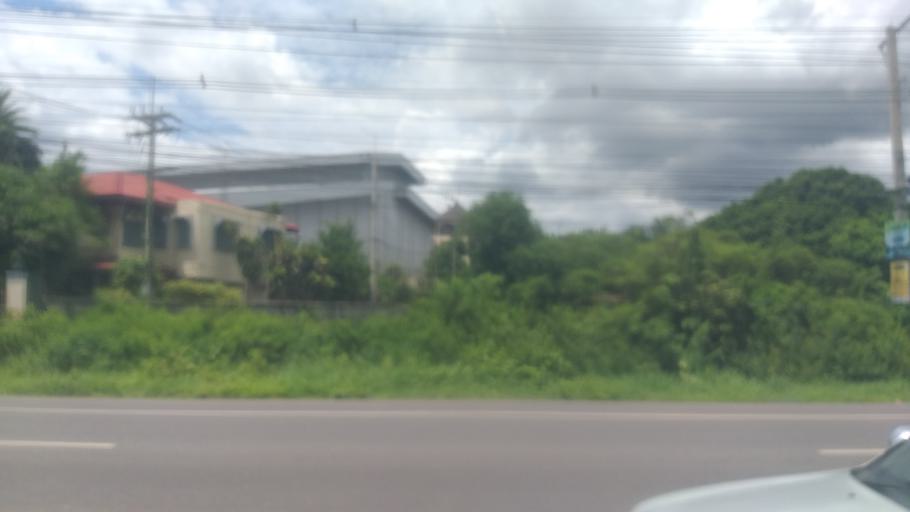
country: TH
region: Nakhon Ratchasima
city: Nakhon Ratchasima
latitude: 15.0851
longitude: 102.1124
